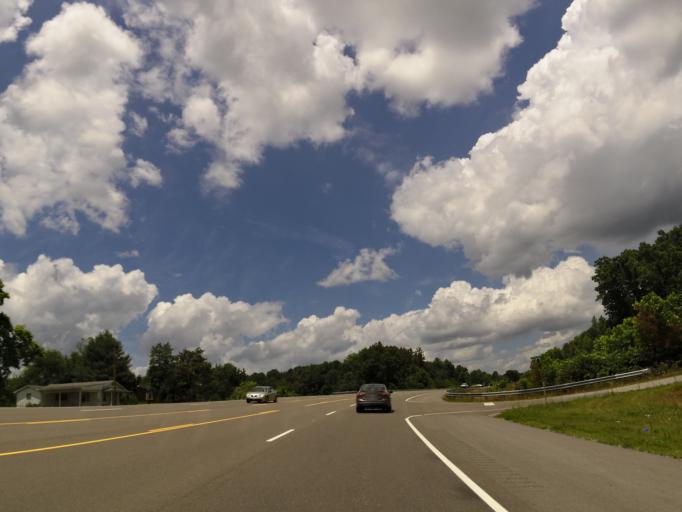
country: US
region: Tennessee
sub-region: Claiborne County
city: Harrogate
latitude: 36.5216
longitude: -83.6159
